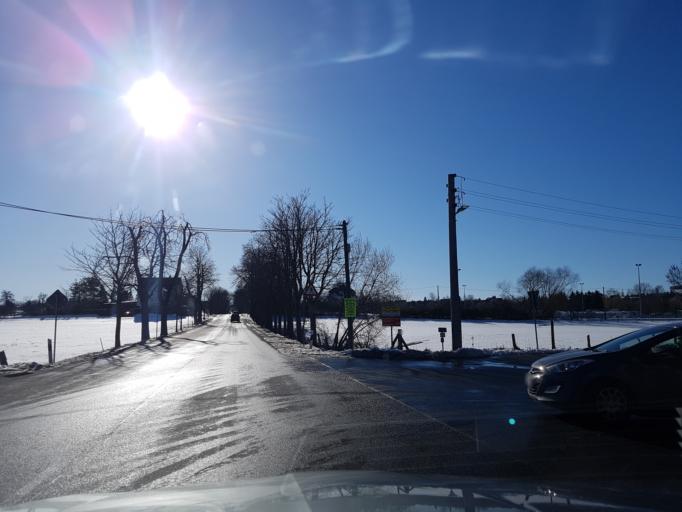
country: DE
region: Saxony
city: Moritzburg
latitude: 51.1306
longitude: 13.6855
